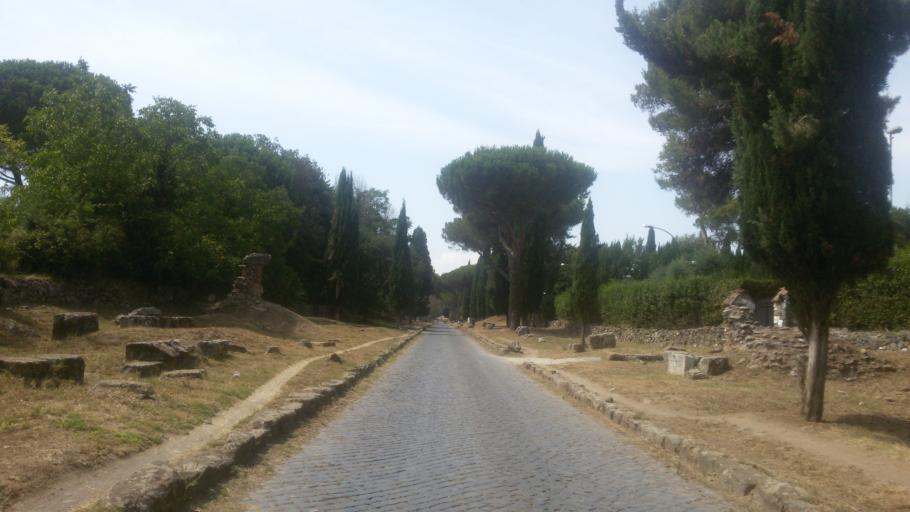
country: IT
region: Latium
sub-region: Citta metropolitana di Roma Capitale
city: Rome
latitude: 41.8323
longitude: 12.5428
